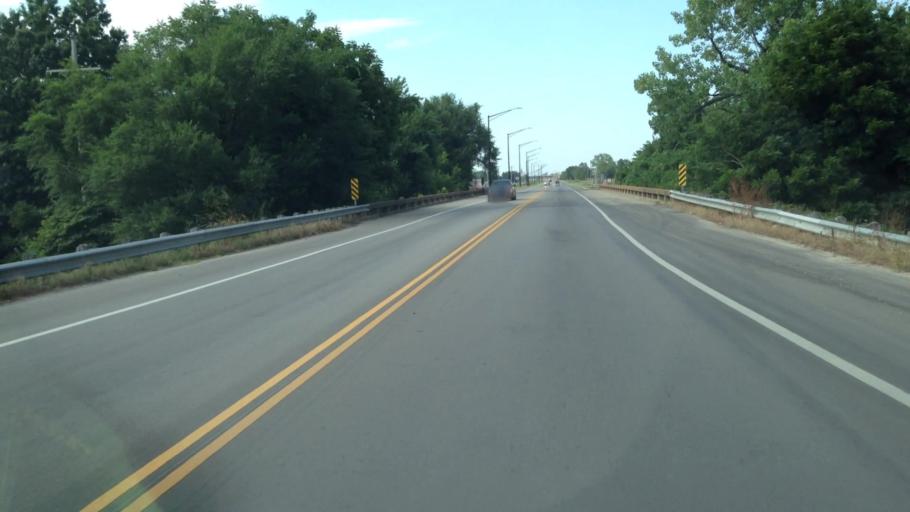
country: US
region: Kansas
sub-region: Labette County
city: Parsons
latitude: 37.3504
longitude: -95.2591
